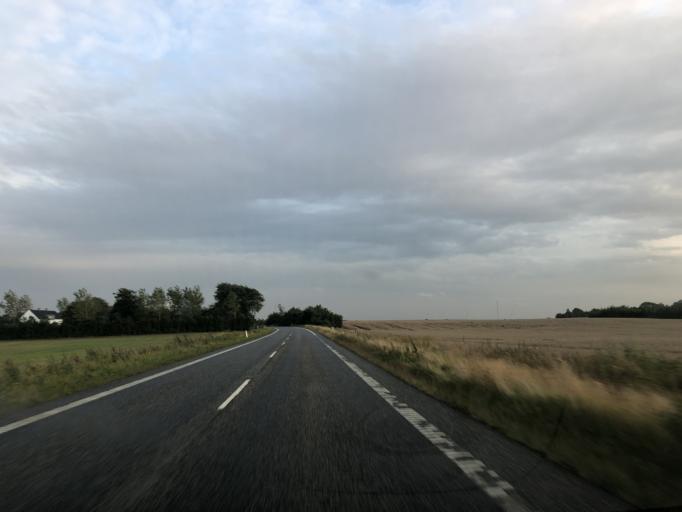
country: DK
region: Central Jutland
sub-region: Holstebro Kommune
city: Vinderup
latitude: 56.6039
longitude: 8.8777
